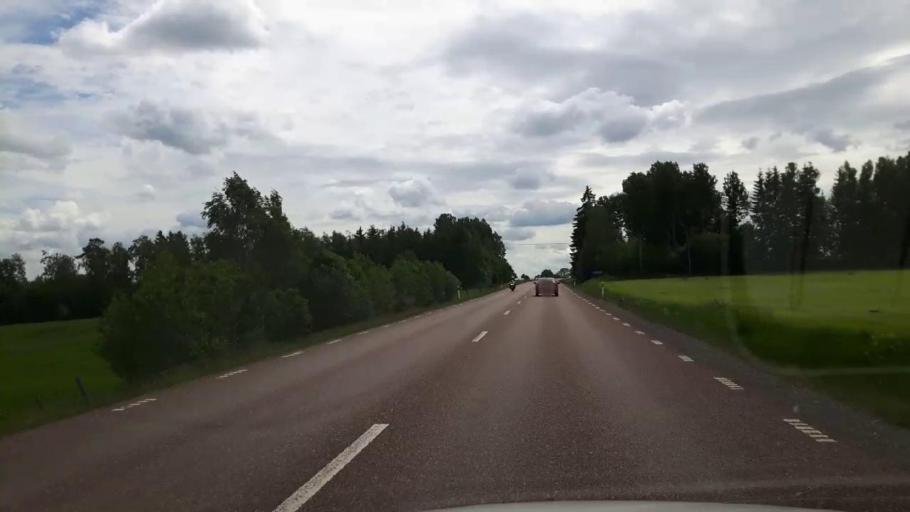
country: SE
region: Dalarna
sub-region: Hedemora Kommun
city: Hedemora
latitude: 60.3054
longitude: 15.9750
